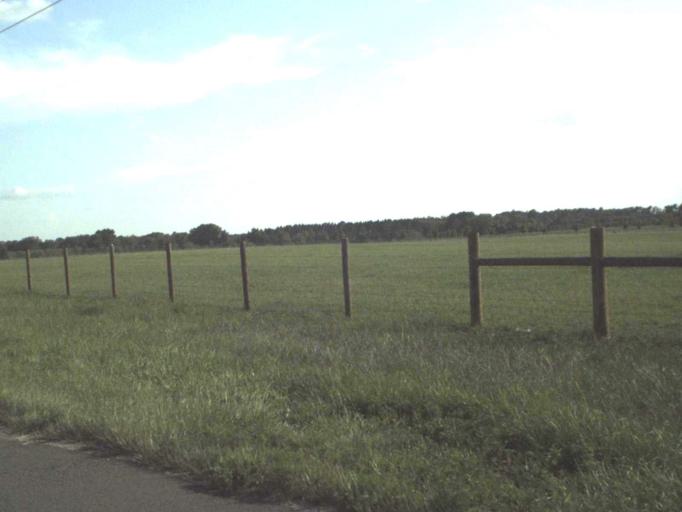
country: US
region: Florida
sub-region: Lake County
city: Groveland
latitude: 28.4834
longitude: -81.8361
